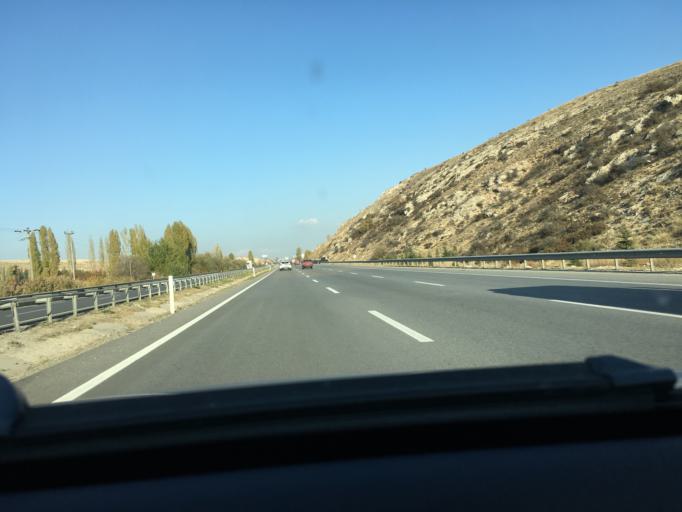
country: TR
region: Ankara
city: Temelli
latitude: 39.7793
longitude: 32.5055
